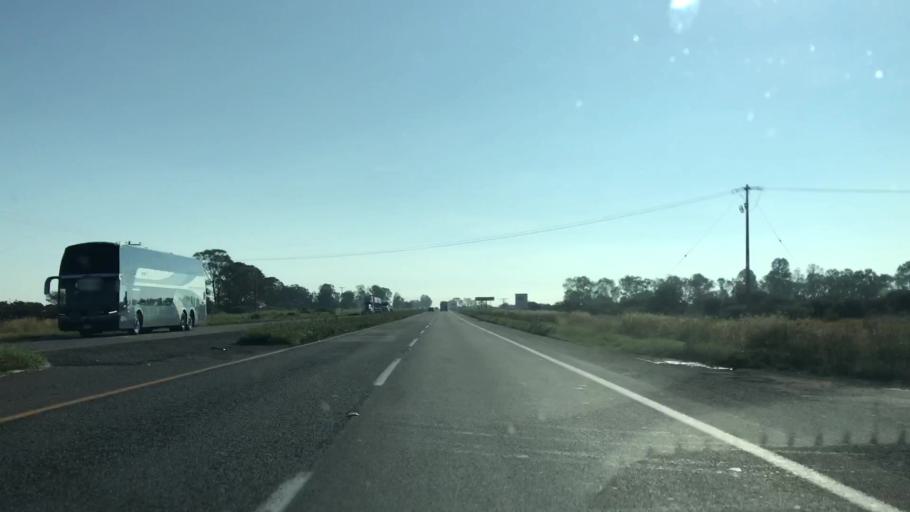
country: MX
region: Jalisco
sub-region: Lagos de Moreno
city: Cristeros [Fraccionamiento]
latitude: 21.2976
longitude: -102.1313
